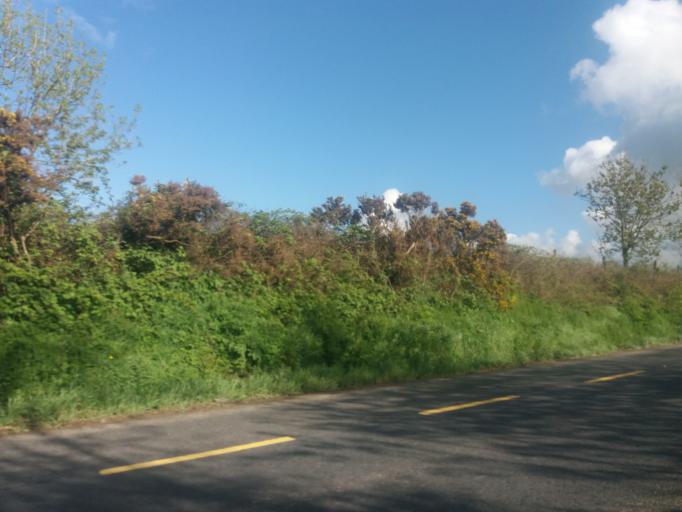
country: IE
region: Leinster
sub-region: Loch Garman
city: Ferns
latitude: 52.5575
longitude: -6.5337
